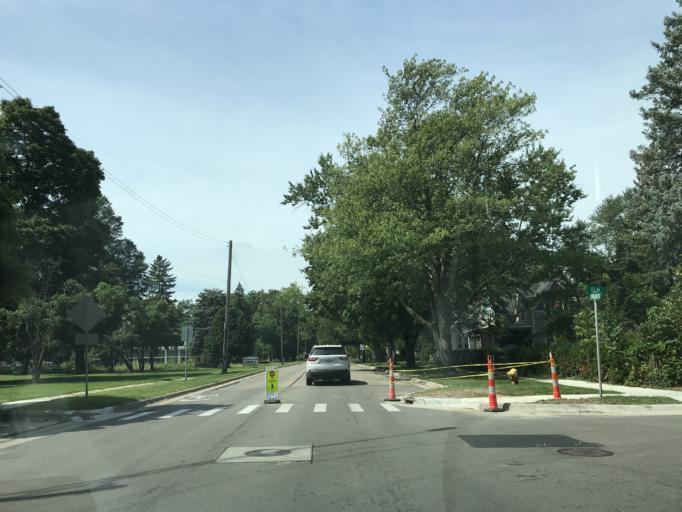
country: US
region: Michigan
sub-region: Washtenaw County
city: Ypsilanti
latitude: 42.2410
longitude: -83.6270
